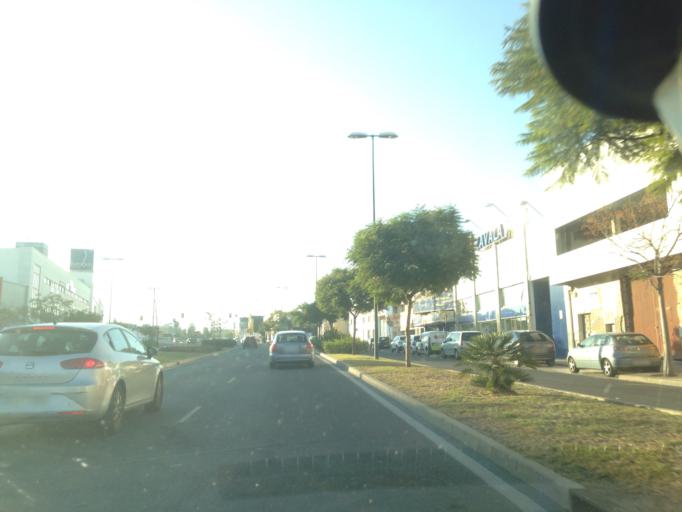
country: ES
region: Andalusia
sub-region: Provincia de Malaga
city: Malaga
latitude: 36.7076
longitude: -4.4757
